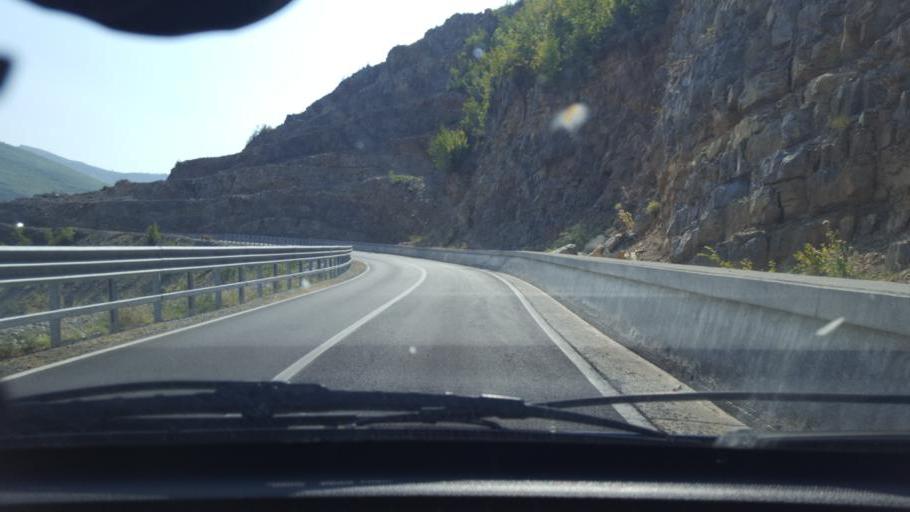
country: AL
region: Shkoder
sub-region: Rrethi i Malesia e Madhe
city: Kastrat
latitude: 42.4128
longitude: 19.5037
